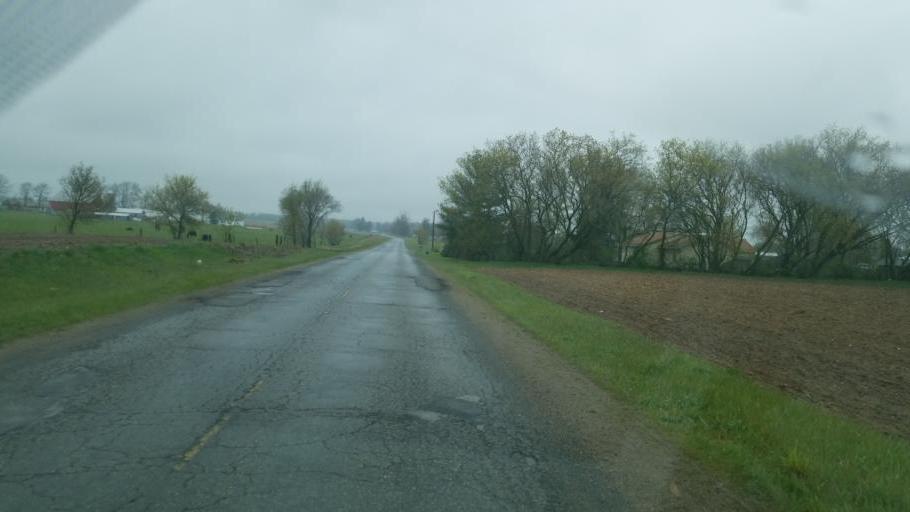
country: US
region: Michigan
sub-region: Mecosta County
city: Canadian Lakes
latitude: 43.5454
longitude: -85.3427
